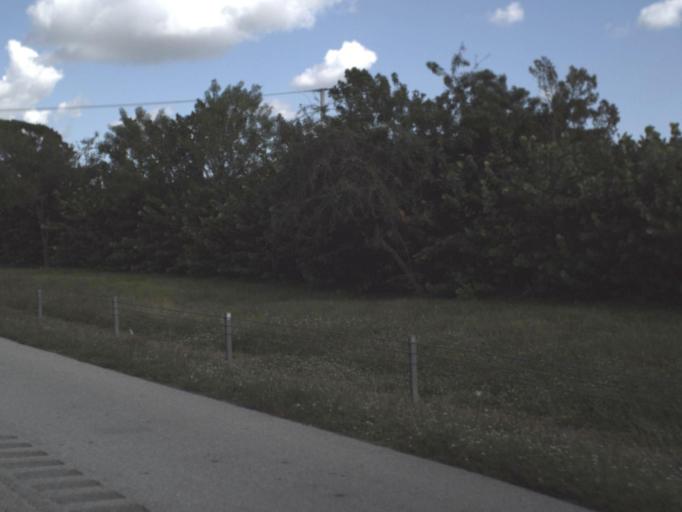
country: US
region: Florida
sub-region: Palm Beach County
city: Boca Pointe
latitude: 26.3567
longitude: -80.1705
